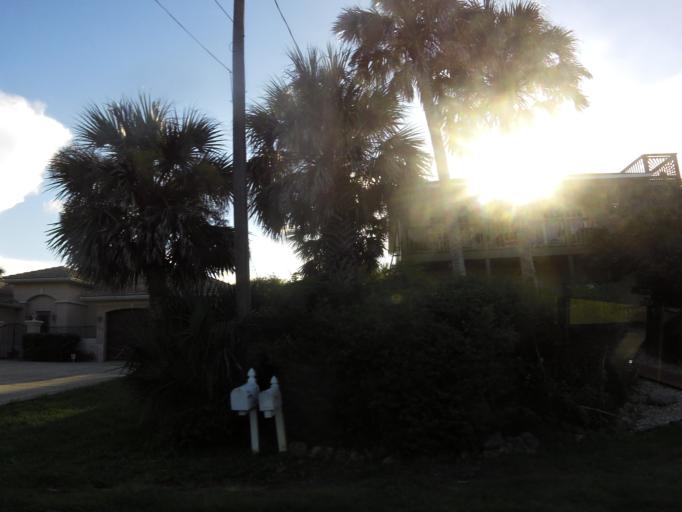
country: US
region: Florida
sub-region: Flagler County
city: Flagler Beach
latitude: 29.4696
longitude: -81.1230
